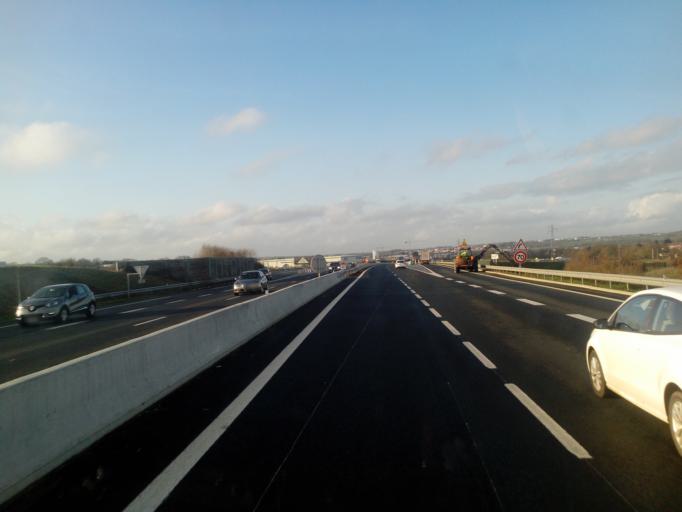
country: FR
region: Pays de la Loire
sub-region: Departement de Maine-et-Loire
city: Cholet
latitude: 47.0340
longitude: -0.9001
